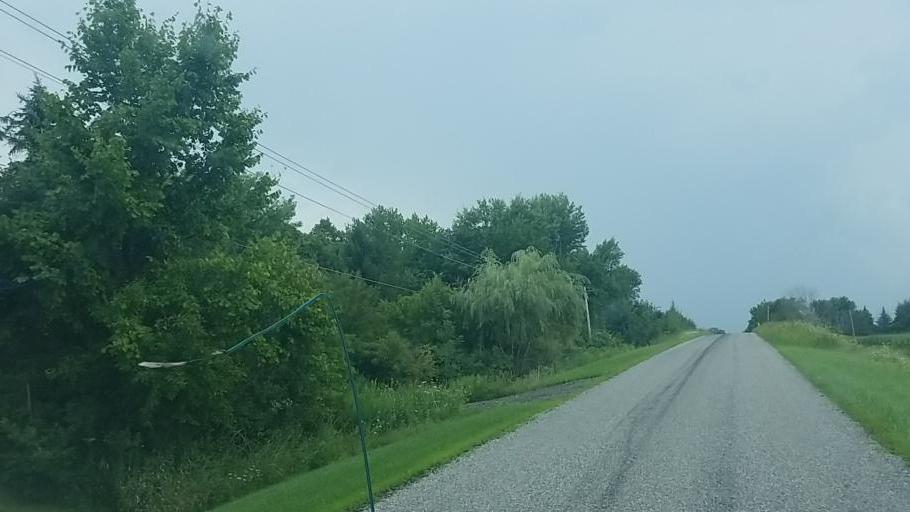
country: US
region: Ohio
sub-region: Medina County
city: Lodi
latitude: 40.9990
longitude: -82.0058
